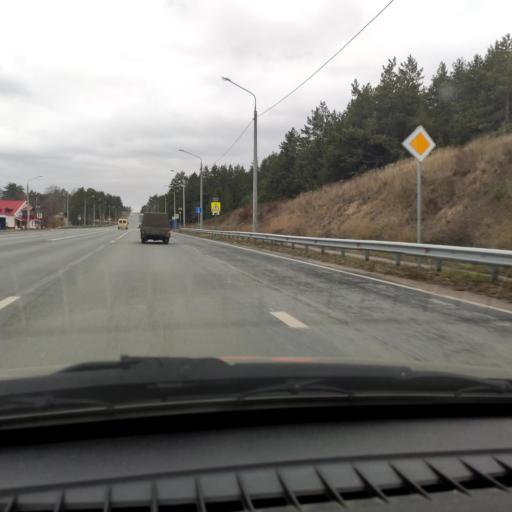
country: RU
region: Samara
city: Volzhskiy
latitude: 53.4376
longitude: 50.1110
